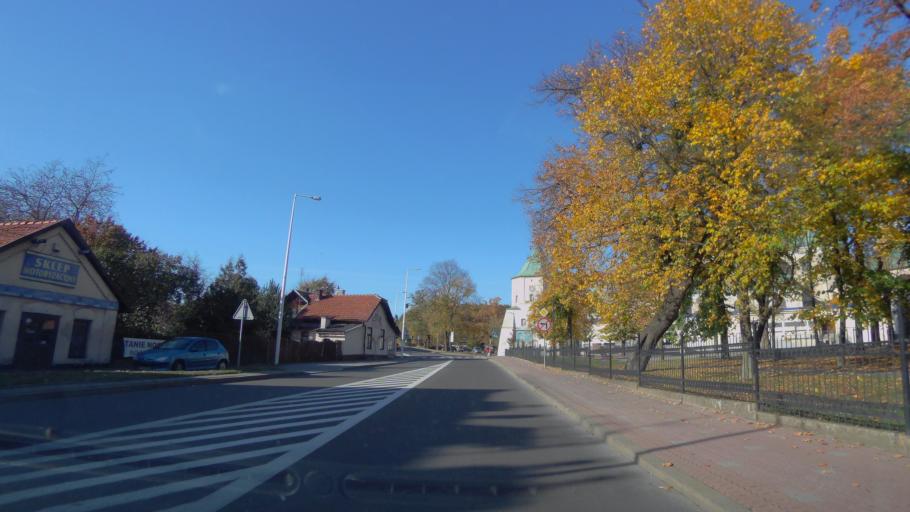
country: PL
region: Subcarpathian Voivodeship
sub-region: Powiat lezajski
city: Lezajsk
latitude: 50.2690
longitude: 22.4085
